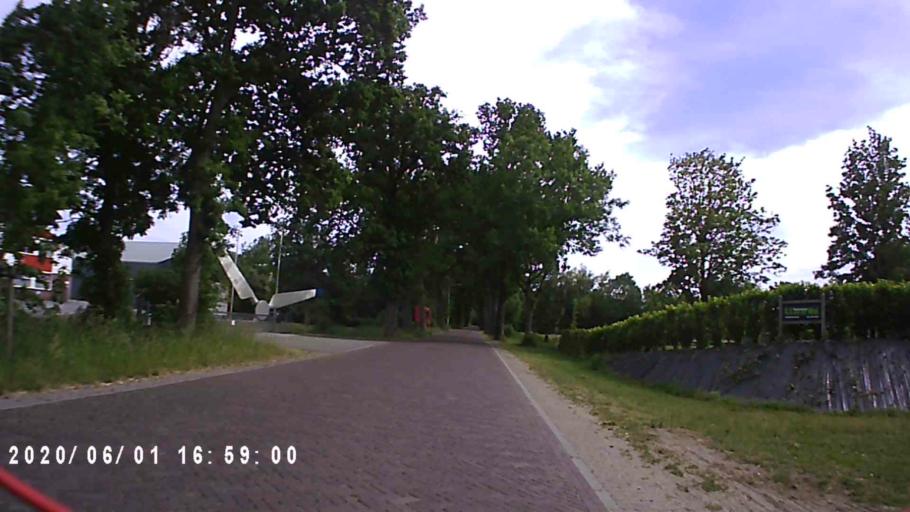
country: NL
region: Friesland
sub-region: Gemeente Tytsjerksteradiel
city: Hurdegaryp
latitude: 53.1875
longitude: 5.9274
